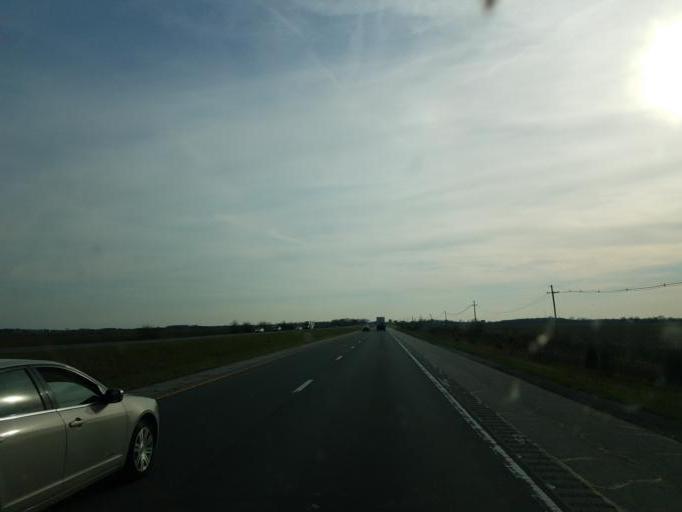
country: US
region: Ohio
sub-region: Fayette County
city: Jeffersonville
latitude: 39.6785
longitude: -83.4906
